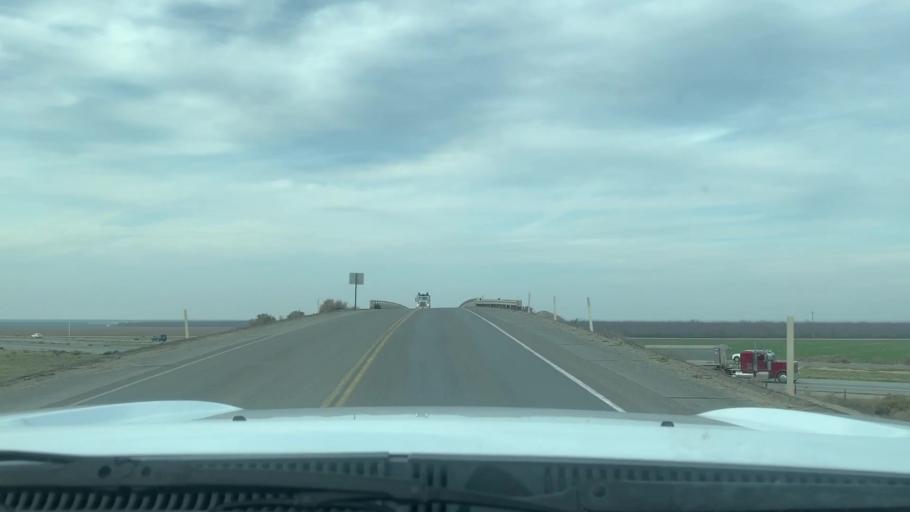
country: US
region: California
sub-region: Kern County
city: Buttonwillow
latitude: 35.4543
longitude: -119.4749
